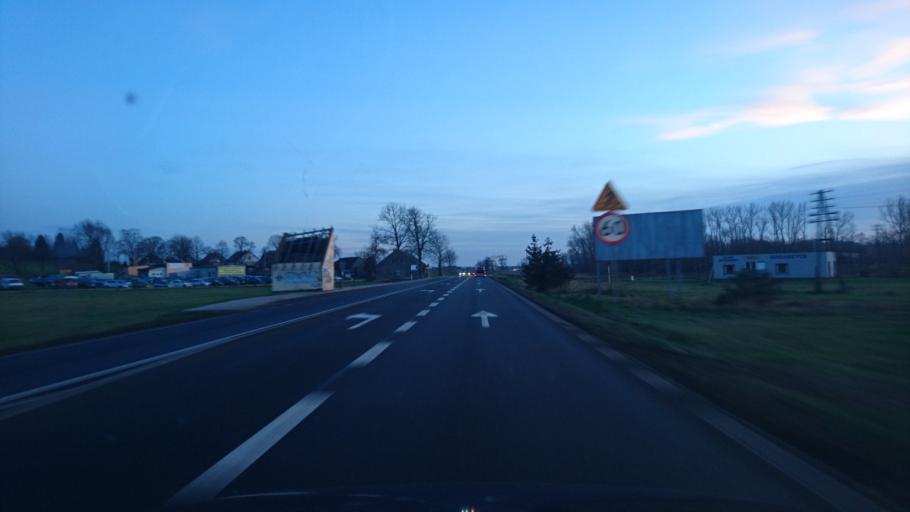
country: PL
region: Greater Poland Voivodeship
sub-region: Powiat ostrzeszowski
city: Ostrzeszow
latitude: 51.3882
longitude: 17.9473
